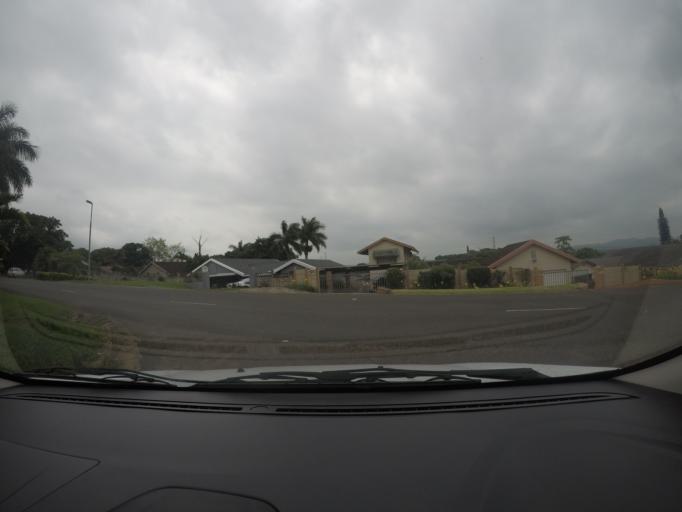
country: ZA
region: KwaZulu-Natal
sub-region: uThungulu District Municipality
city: Empangeni
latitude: -28.7356
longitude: 31.8995
